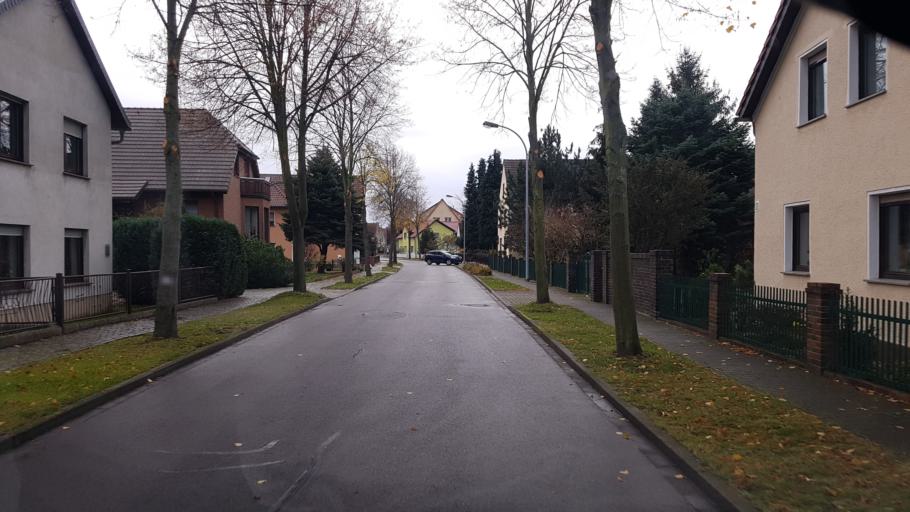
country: DE
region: Brandenburg
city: Tettau
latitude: 51.4334
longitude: 13.7259
